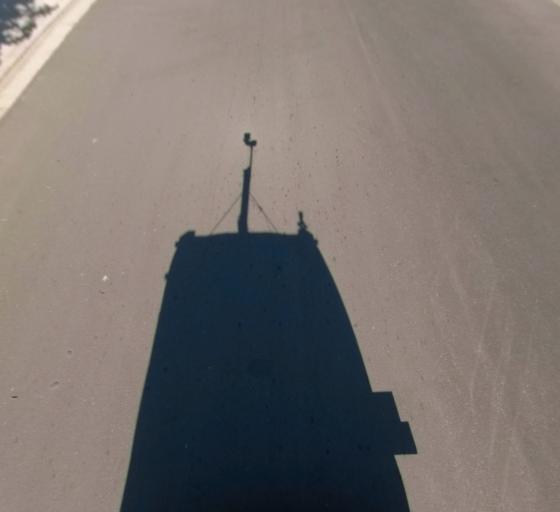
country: US
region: California
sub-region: Madera County
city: Madera
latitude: 36.9500
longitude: -120.0515
